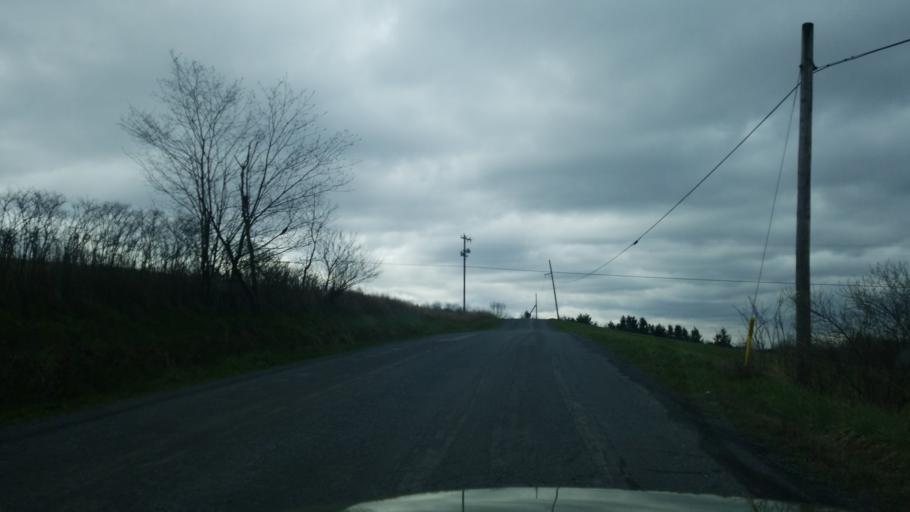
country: US
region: Pennsylvania
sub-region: Clearfield County
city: Clearfield
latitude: 41.0826
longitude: -78.3968
